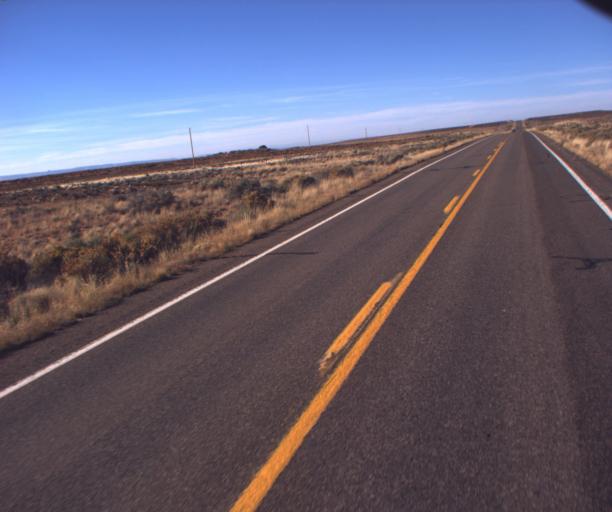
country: US
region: Arizona
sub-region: Coconino County
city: LeChee
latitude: 36.7147
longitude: -111.2734
